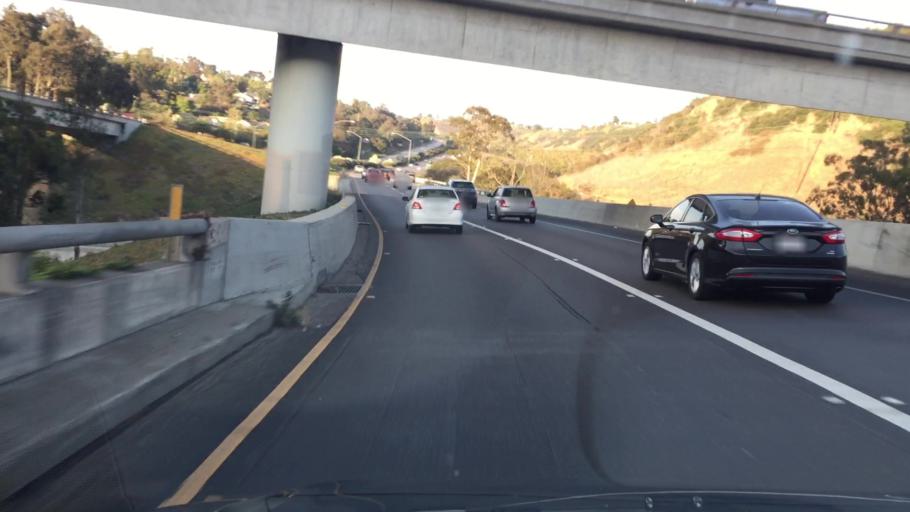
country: US
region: California
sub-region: San Diego County
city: La Jolla
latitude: 32.8375
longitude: -117.2341
